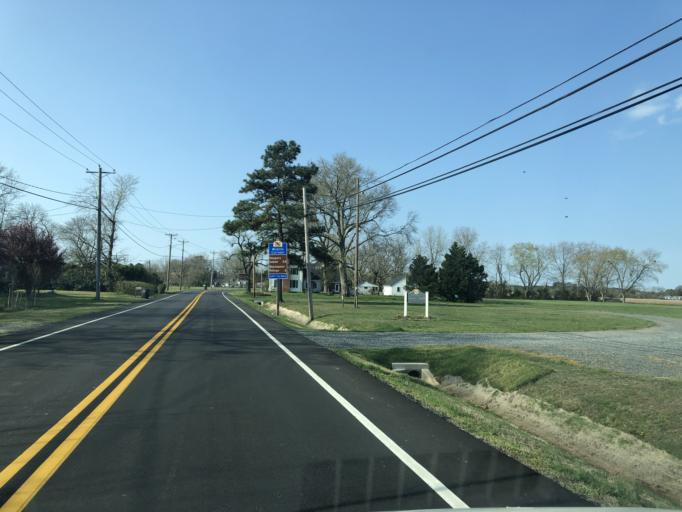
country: US
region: Maryland
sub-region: Dorchester County
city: Algonquin
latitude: 38.5066
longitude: -76.1488
